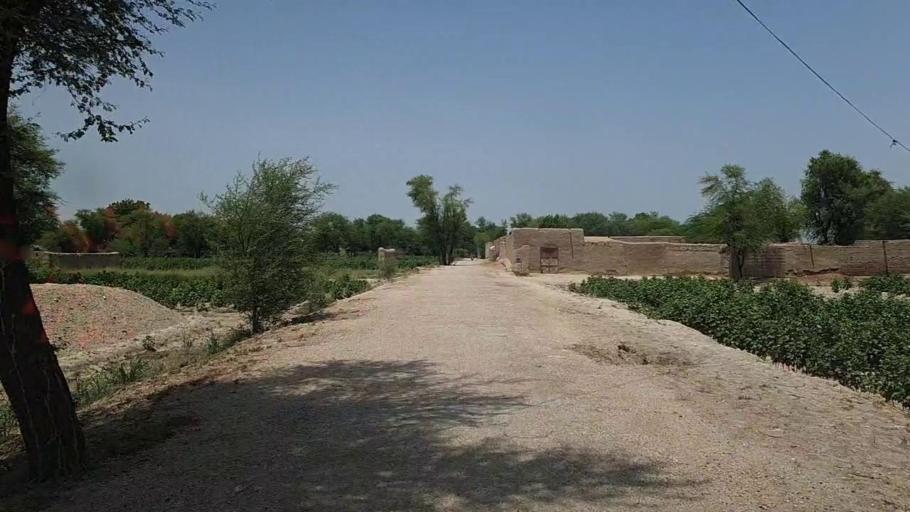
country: PK
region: Sindh
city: Pad Idan
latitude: 26.7534
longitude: 68.3107
